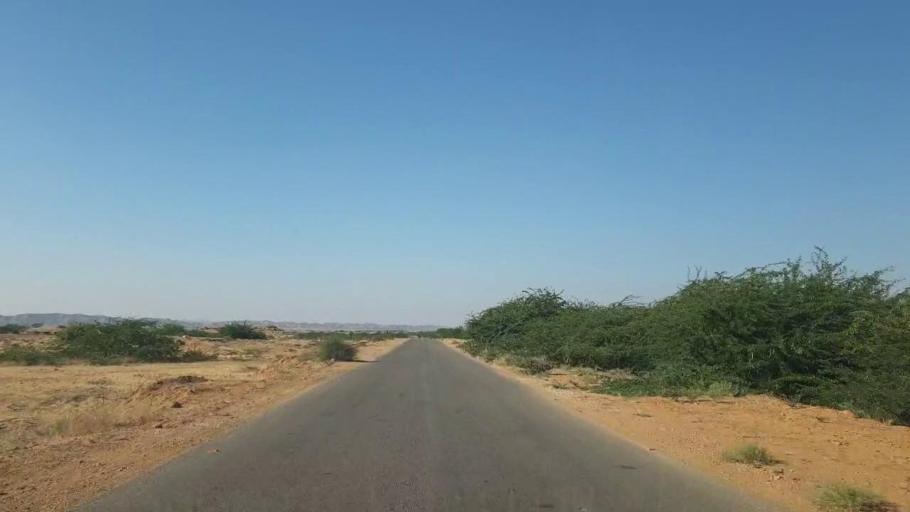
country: PK
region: Sindh
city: Malir Cantonment
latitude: 25.2727
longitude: 67.5913
